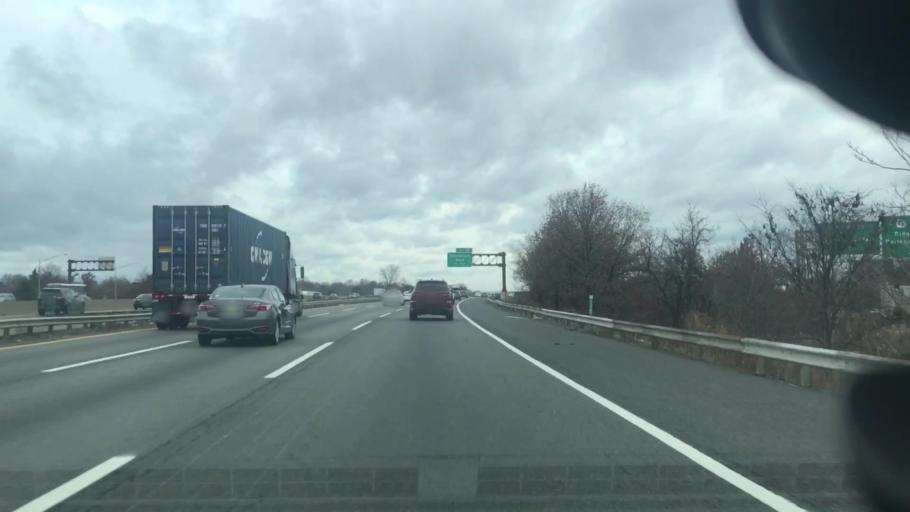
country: US
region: New Jersey
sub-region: Bergen County
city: Ridgefield
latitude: 40.8442
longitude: -74.0176
